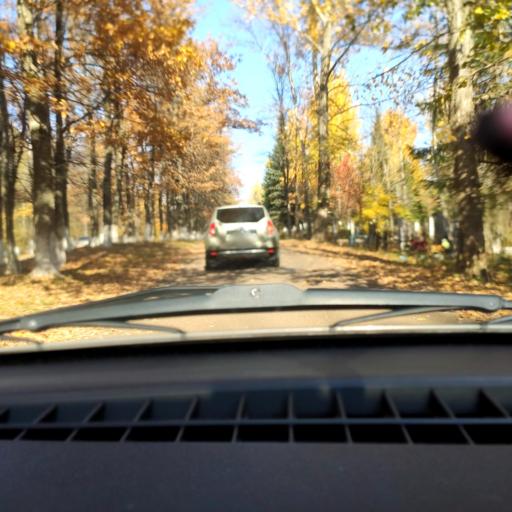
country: RU
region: Bashkortostan
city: Mikhaylovka
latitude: 54.8051
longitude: 55.8634
